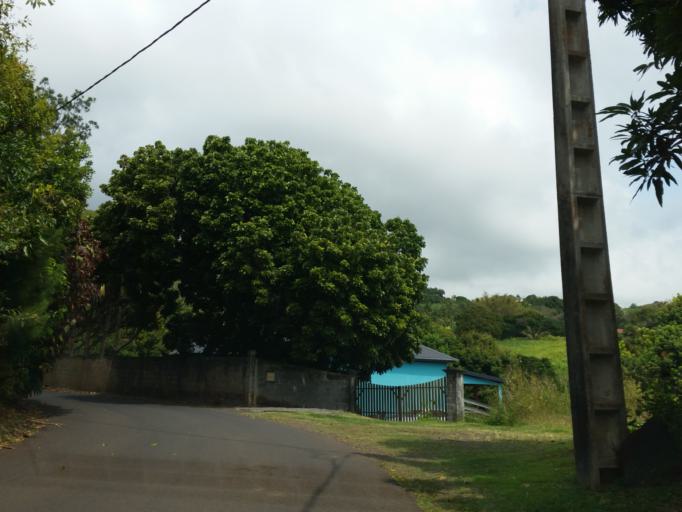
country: RE
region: Reunion
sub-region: Reunion
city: Sainte-Suzanne
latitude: -20.9228
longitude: 55.6092
